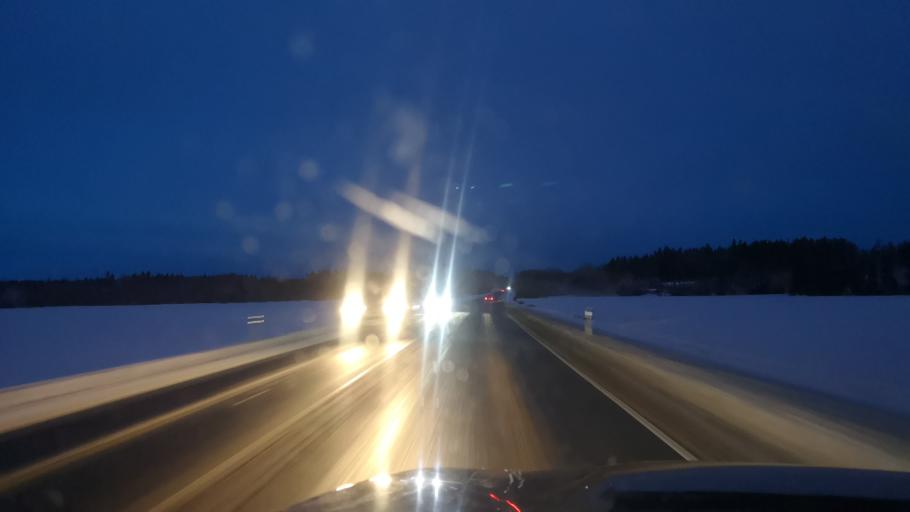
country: FI
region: Varsinais-Suomi
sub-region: Loimaa
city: Loimaa
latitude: 60.8636
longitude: 23.0506
